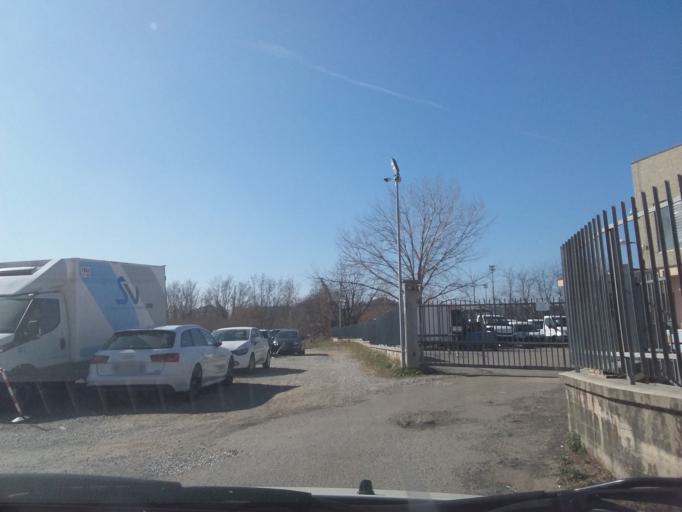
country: IT
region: Piedmont
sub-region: Provincia di Torino
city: Rivoli
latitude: 45.0647
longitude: 7.5336
